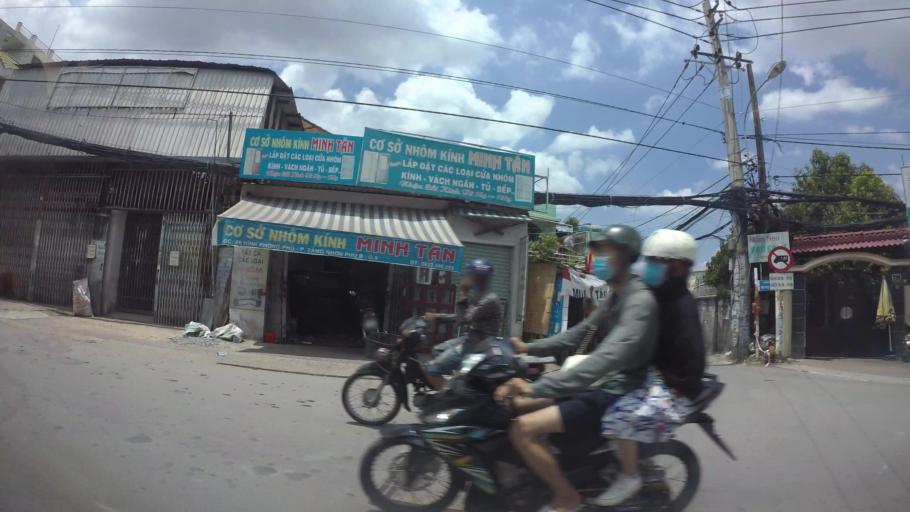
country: VN
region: Ho Chi Minh City
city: Quan Chin
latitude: 10.8395
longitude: 106.7801
